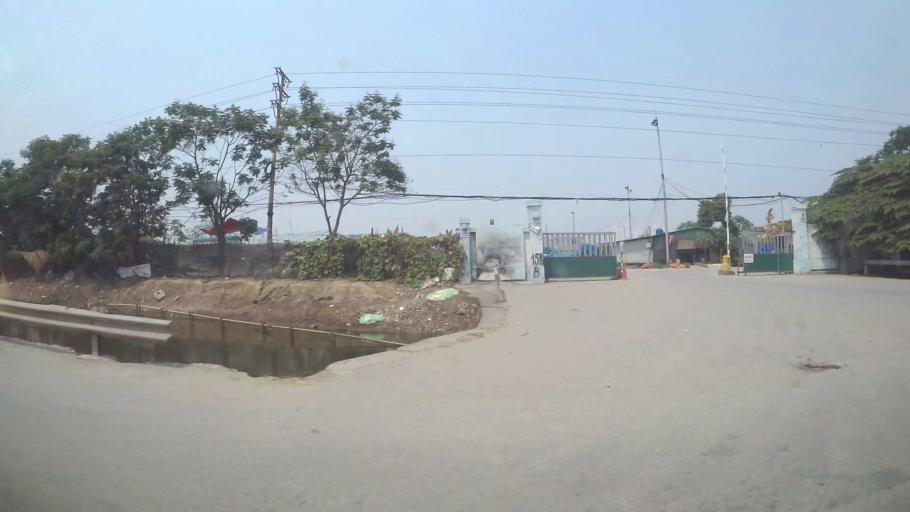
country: VN
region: Ha Noi
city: Van Dien
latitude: 20.9543
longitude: 105.8133
